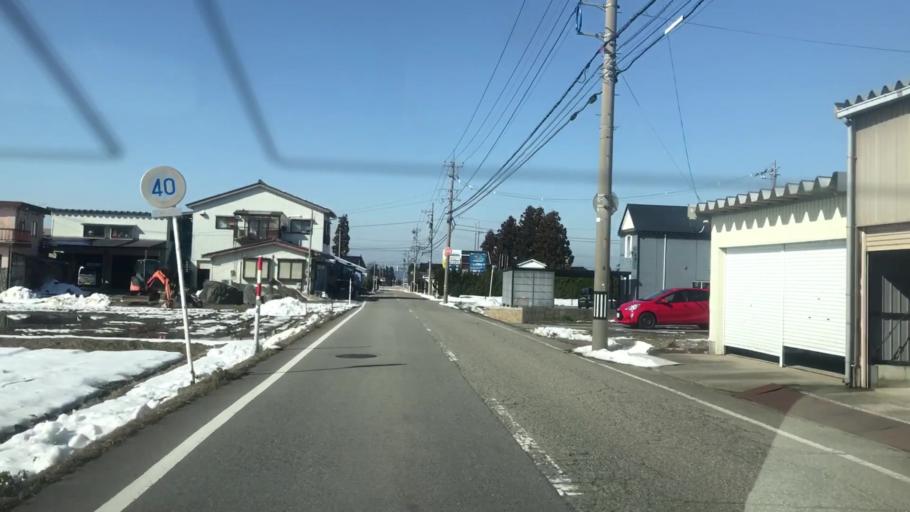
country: JP
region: Toyama
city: Toyama-shi
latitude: 36.6263
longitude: 137.2767
